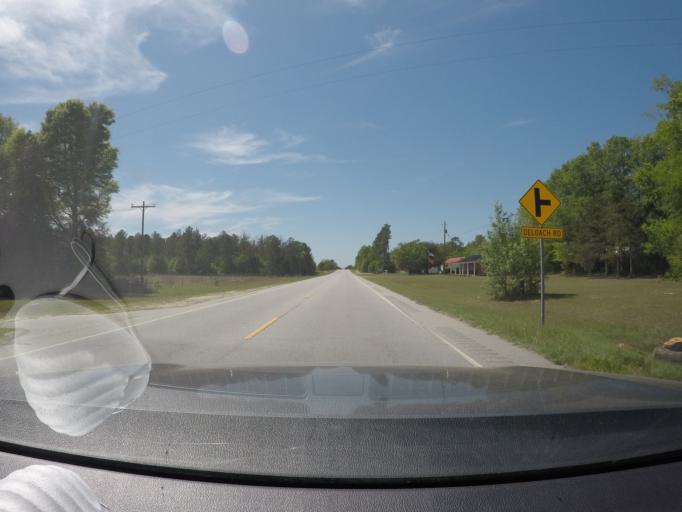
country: US
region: Georgia
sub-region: Bryan County
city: Pembroke
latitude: 32.1462
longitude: -81.7610
